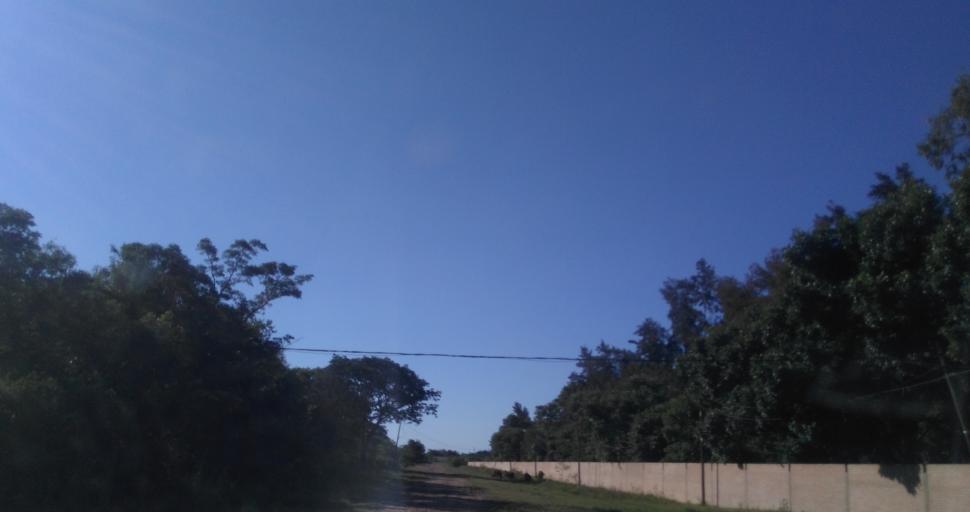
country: AR
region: Chaco
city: Barranqueras
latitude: -27.4344
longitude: -58.9194
